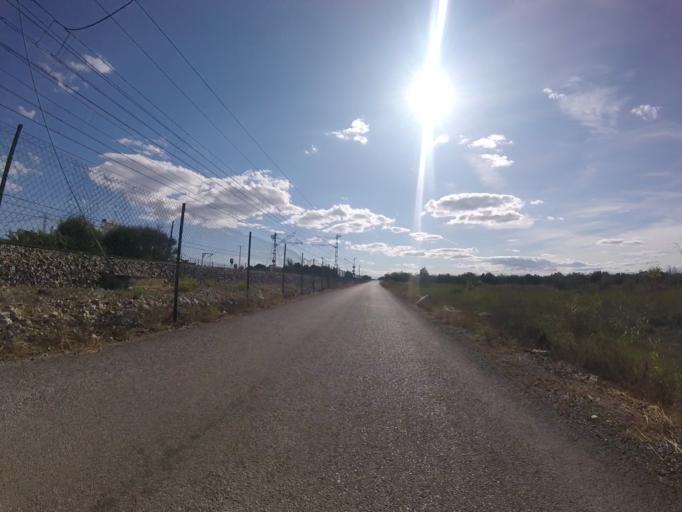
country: ES
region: Valencia
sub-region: Provincia de Castello
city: Alcala de Xivert
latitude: 40.2971
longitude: 0.2258
